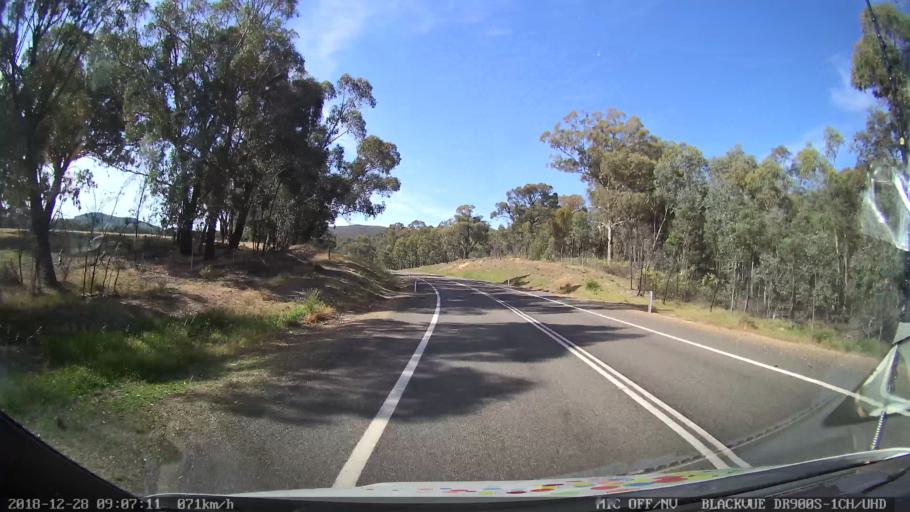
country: AU
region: New South Wales
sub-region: Upper Lachlan Shire
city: Crookwell
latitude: -34.2040
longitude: 149.3445
